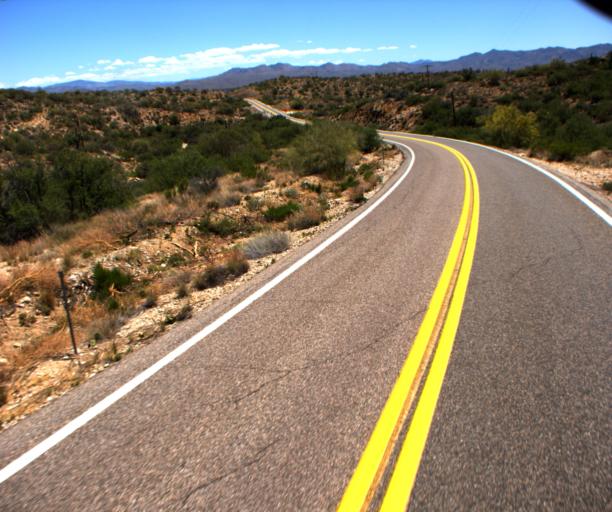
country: US
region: Arizona
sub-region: Yavapai County
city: Bagdad
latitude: 34.5233
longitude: -113.1153
